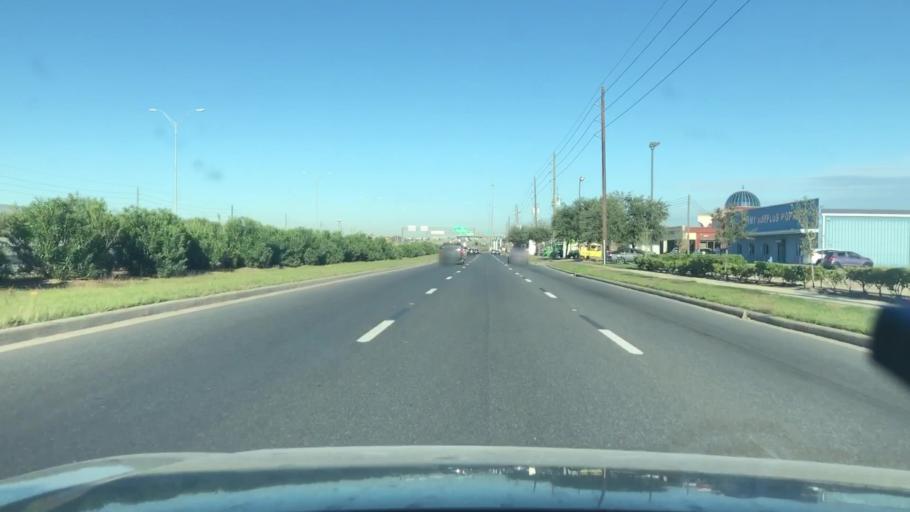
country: US
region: Texas
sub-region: Fort Bend County
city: Missouri City
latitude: 29.6492
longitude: -95.5446
